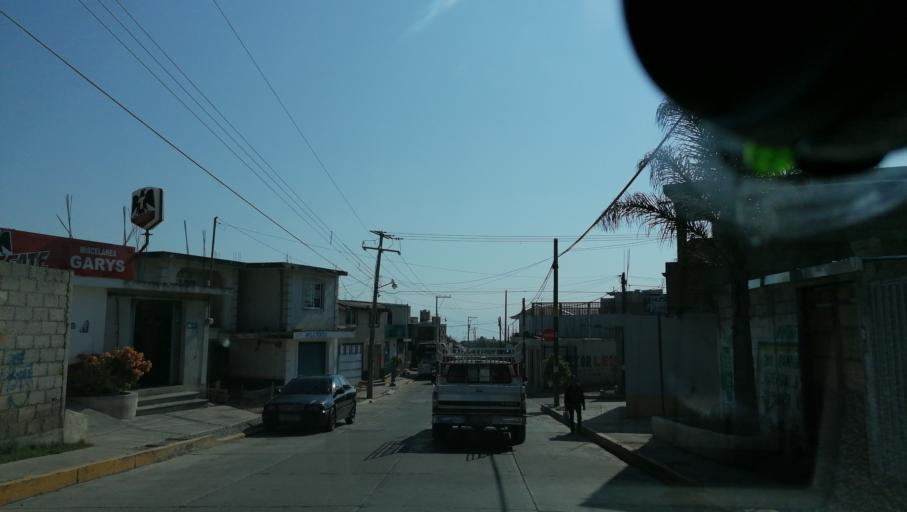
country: MX
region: Puebla
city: Domingo Arenas
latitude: 19.1425
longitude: -98.4553
